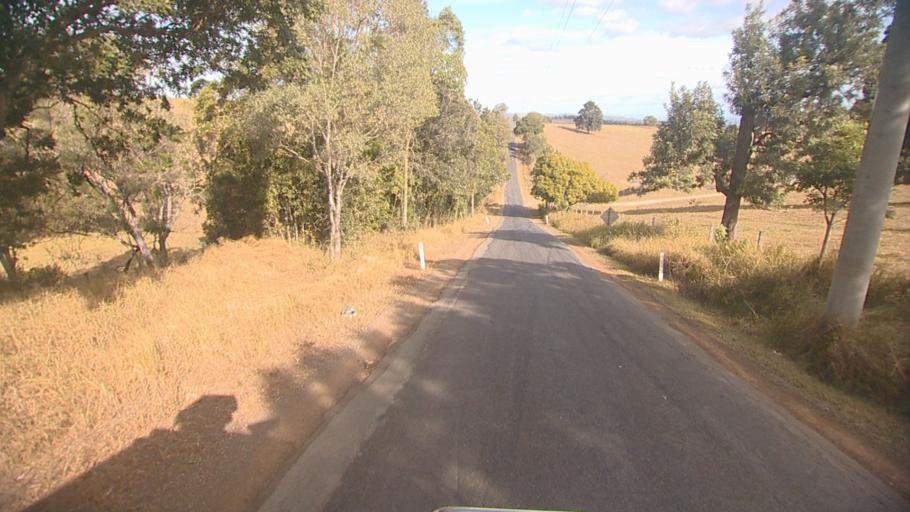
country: AU
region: Queensland
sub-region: Logan
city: Cedar Vale
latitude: -27.9015
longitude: 153.0151
